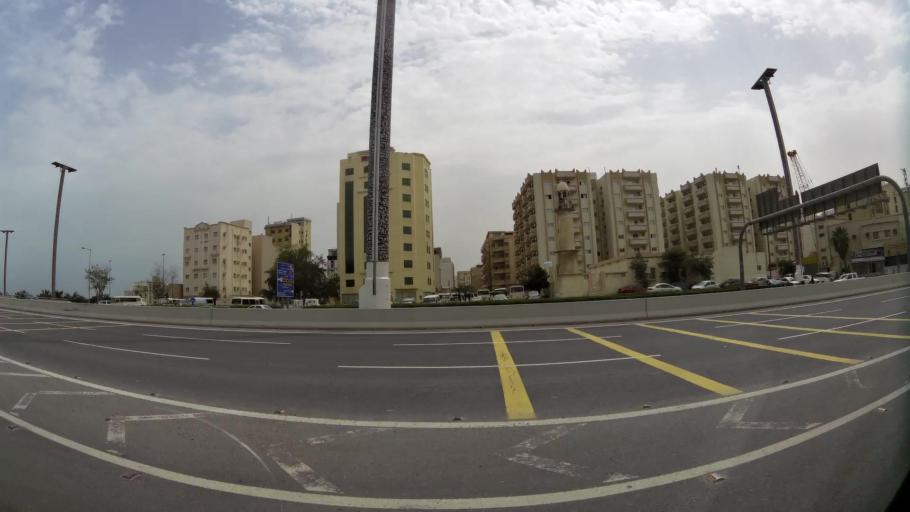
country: QA
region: Baladiyat ad Dawhah
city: Doha
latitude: 25.2838
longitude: 51.5495
